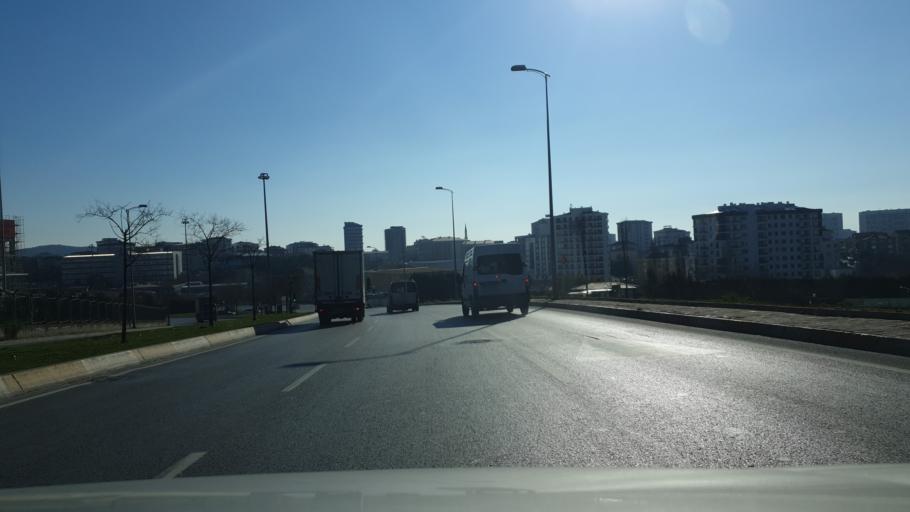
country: TR
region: Istanbul
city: Icmeler
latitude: 40.8766
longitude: 29.3378
